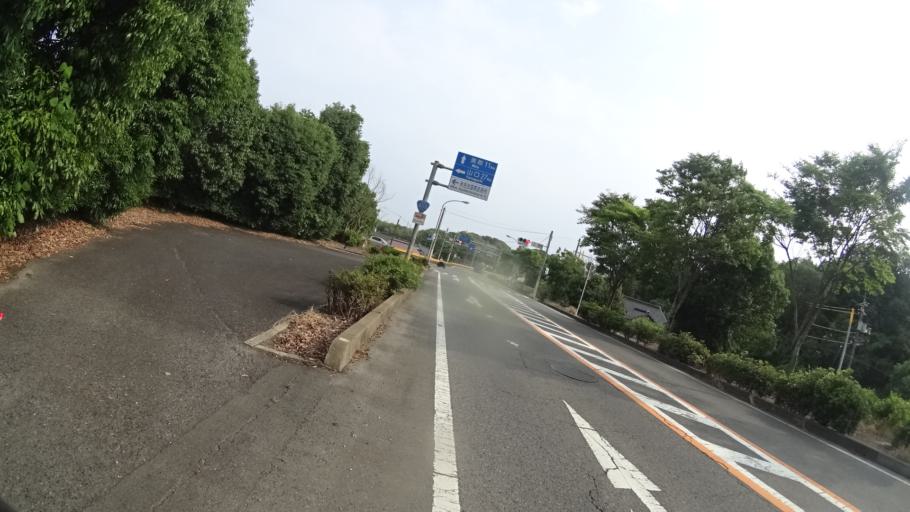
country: JP
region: Yamaguchi
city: Ogori-shimogo
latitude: 34.2104
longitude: 131.2912
